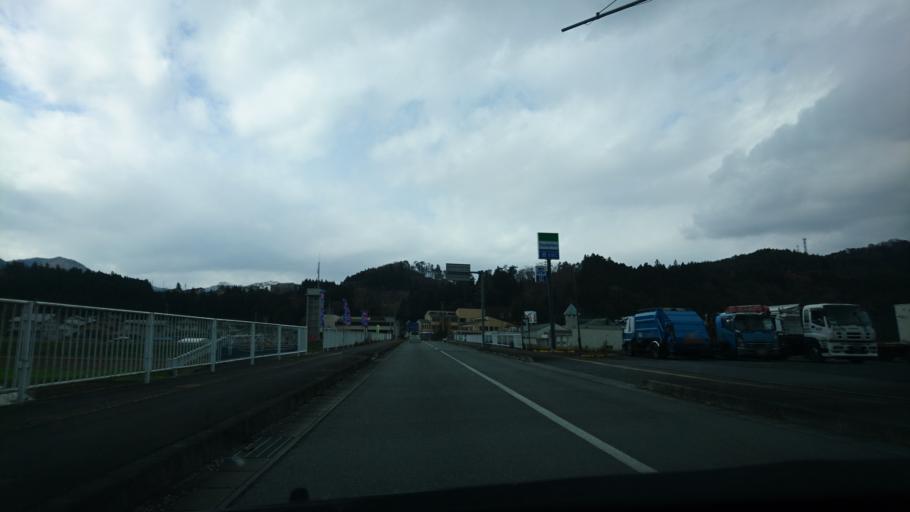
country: JP
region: Iwate
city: Ichinoseki
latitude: 38.9942
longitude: 141.2570
